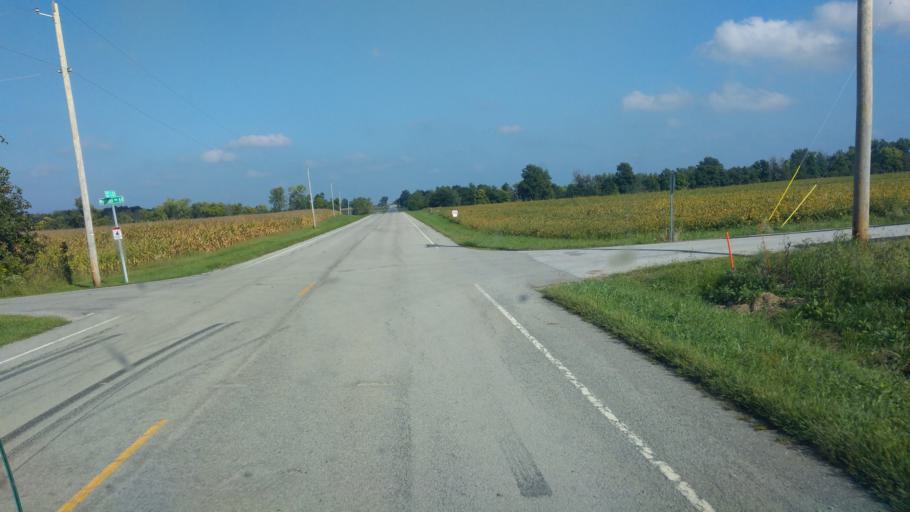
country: US
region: Ohio
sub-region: Hancock County
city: Arlington
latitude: 40.8341
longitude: -83.6707
